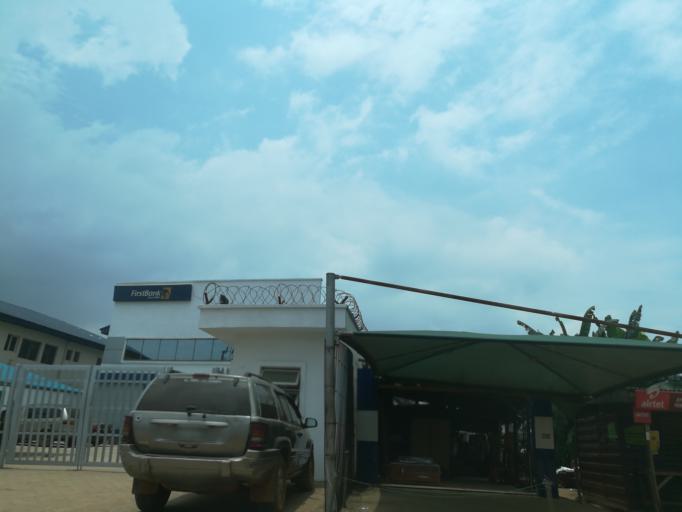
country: NG
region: Lagos
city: Ikorodu
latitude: 6.6210
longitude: 3.5563
